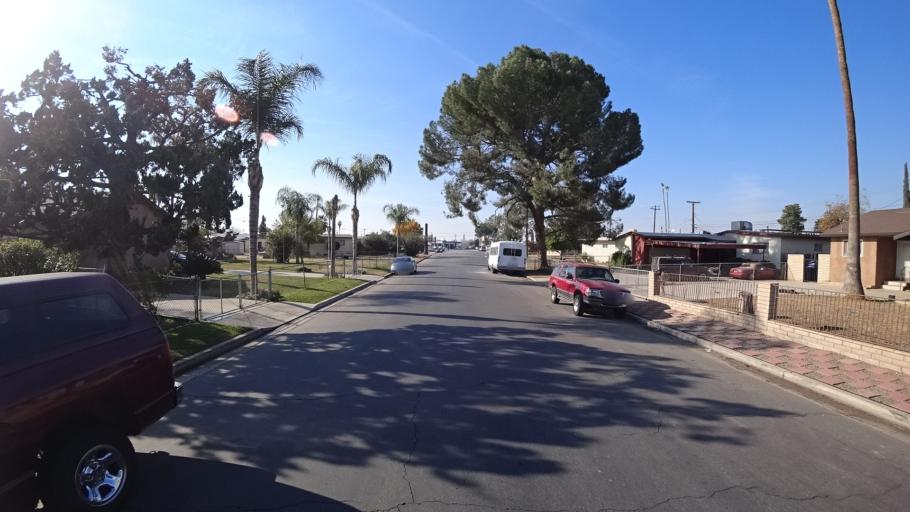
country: US
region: California
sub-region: Kern County
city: Bakersfield
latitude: 35.3289
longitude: -119.0097
